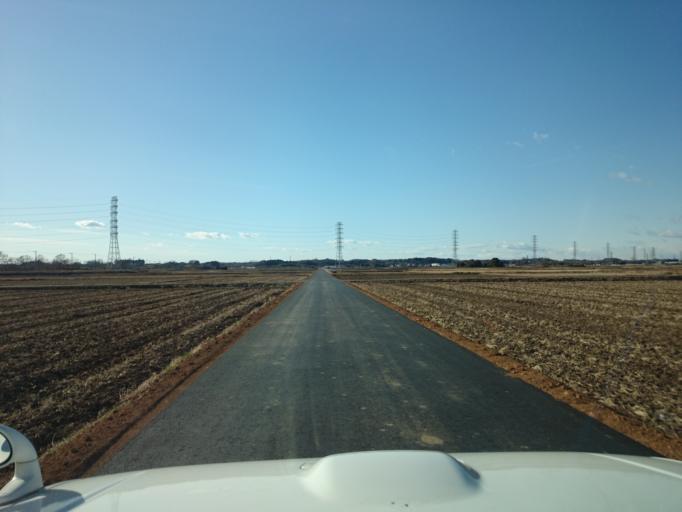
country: JP
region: Ibaraki
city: Tsukuba
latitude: 36.1468
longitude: 140.1135
